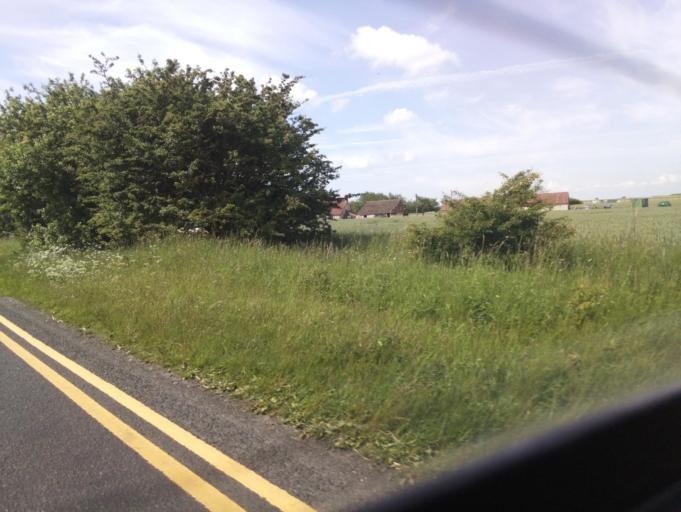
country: GB
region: England
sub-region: Lincolnshire
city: Burton
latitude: 53.3162
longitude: -0.5297
